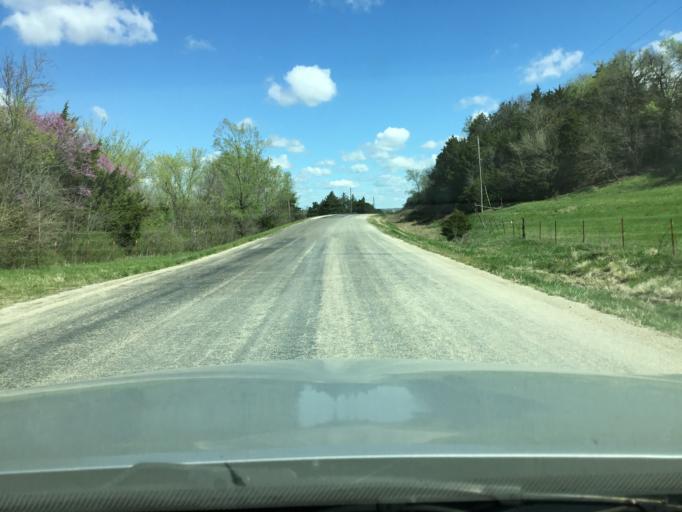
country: US
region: Kansas
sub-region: Anderson County
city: Garnett
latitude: 38.3488
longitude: -95.1258
